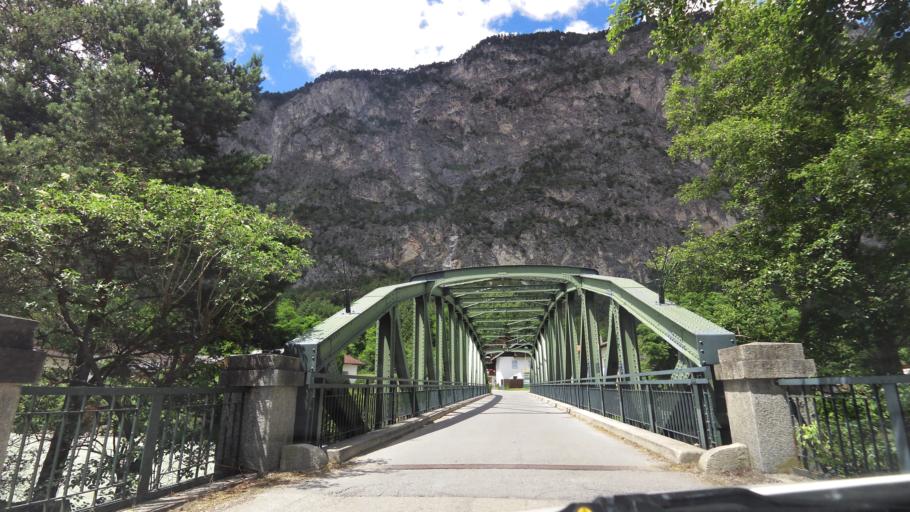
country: AT
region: Tyrol
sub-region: Politischer Bezirk Imst
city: Haiming
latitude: 47.2584
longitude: 10.8752
